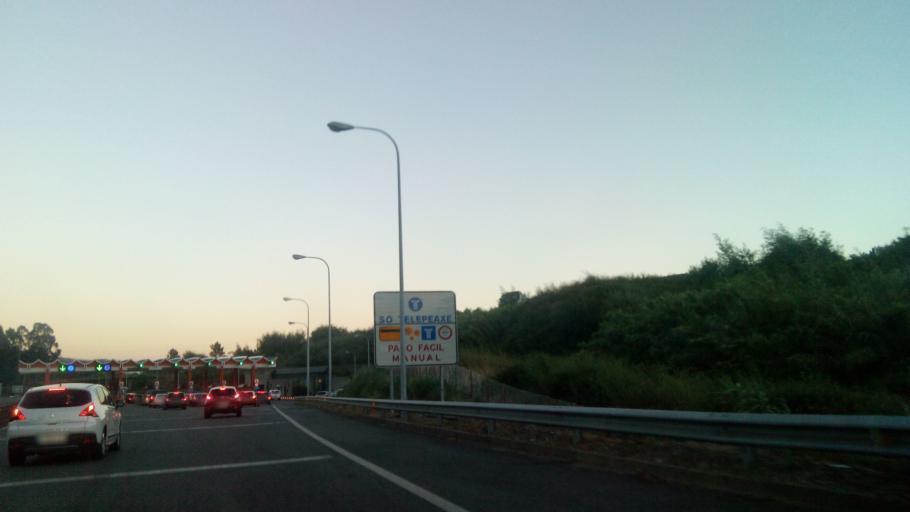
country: ES
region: Galicia
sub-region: Provincia de Pontevedra
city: Pontevedra
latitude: 42.4476
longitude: -8.6496
